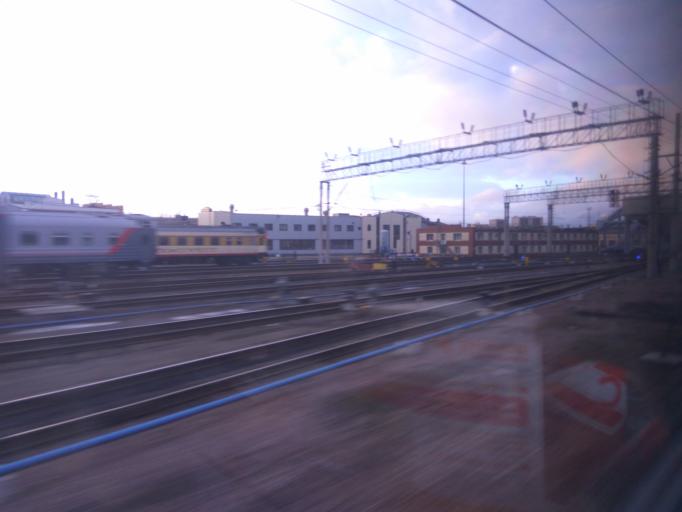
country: RU
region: St.-Petersburg
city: Centralniy
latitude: 59.9119
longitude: 30.3683
